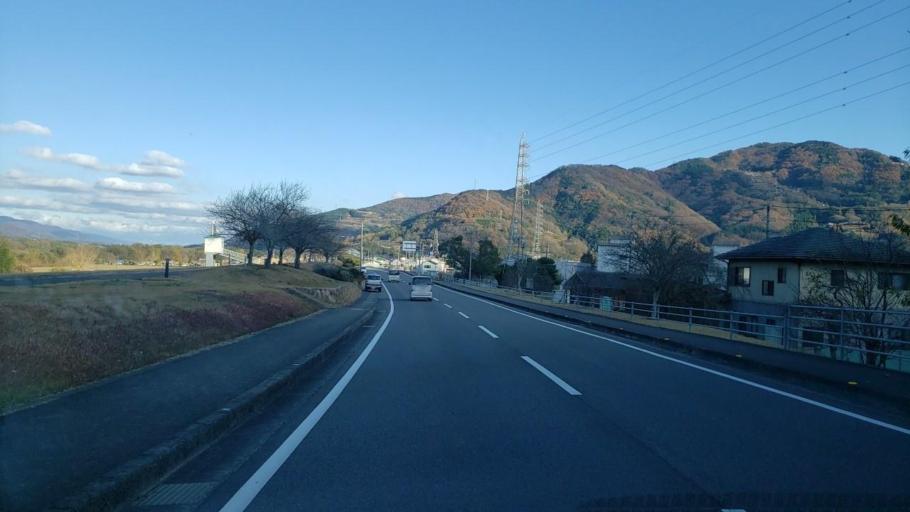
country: JP
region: Tokushima
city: Wakimachi
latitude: 34.0422
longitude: 134.0538
